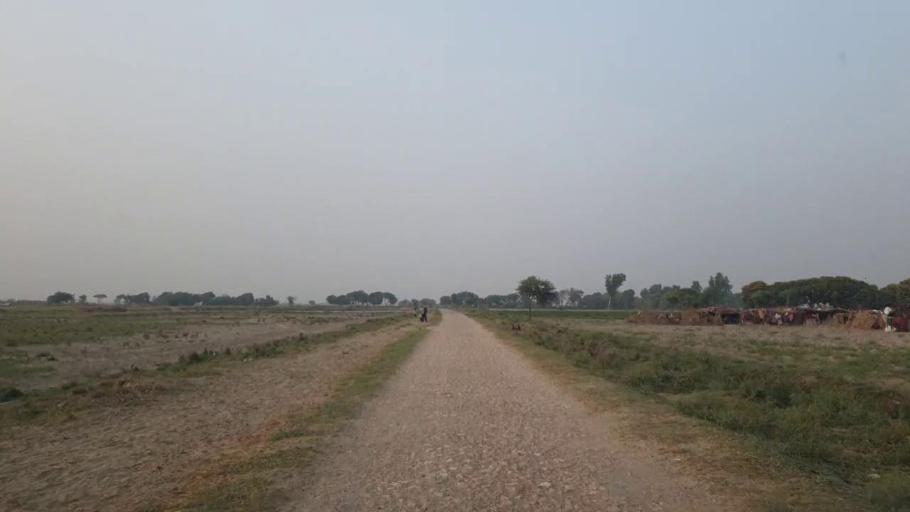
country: PK
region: Sindh
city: Mirpur Batoro
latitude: 24.6609
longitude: 68.3846
